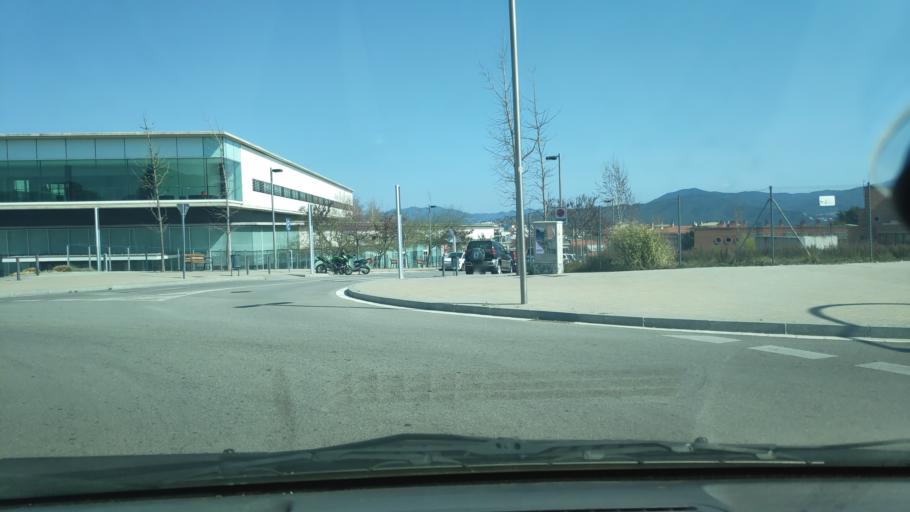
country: ES
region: Catalonia
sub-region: Provincia de Barcelona
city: Mollet del Valles
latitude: 41.5428
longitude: 2.2015
